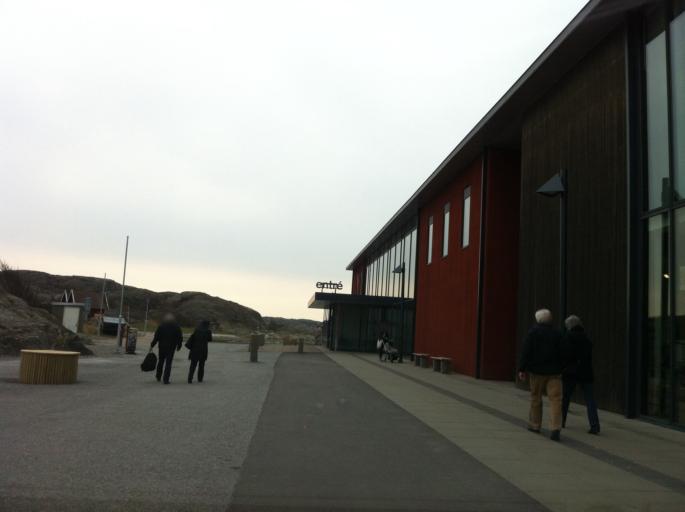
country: SE
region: Vaestra Goetaland
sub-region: Tjorns Kommun
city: Myggenas
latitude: 58.1465
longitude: 11.7071
